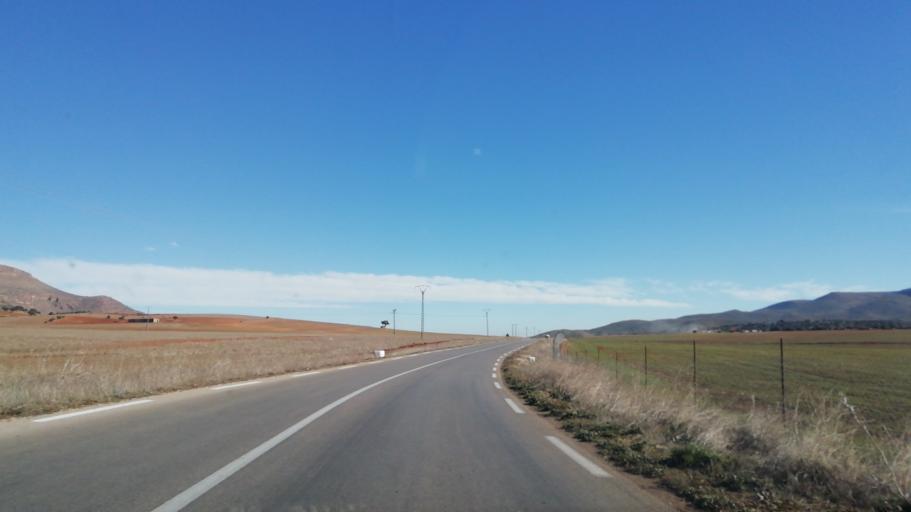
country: DZ
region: Tlemcen
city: Sebdou
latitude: 34.7293
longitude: -1.1846
